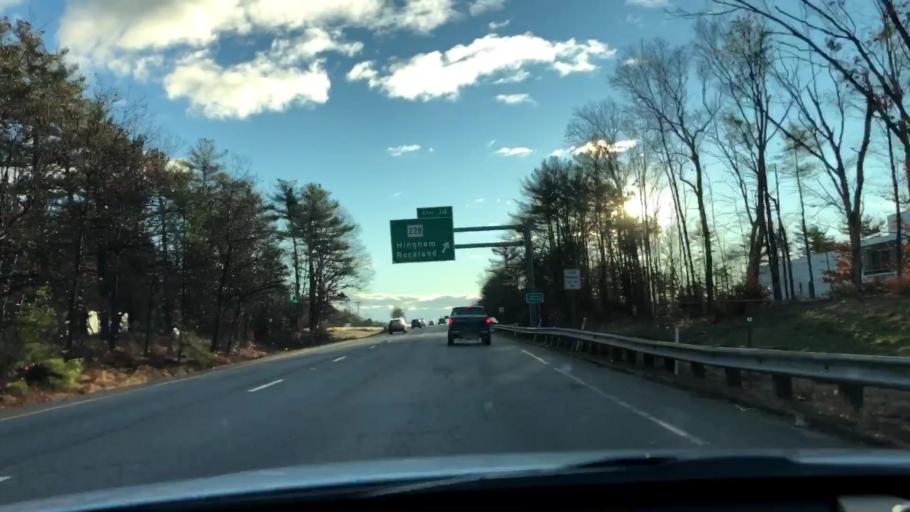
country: US
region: Massachusetts
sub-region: Plymouth County
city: Rockland
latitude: 42.1682
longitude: -70.8998
